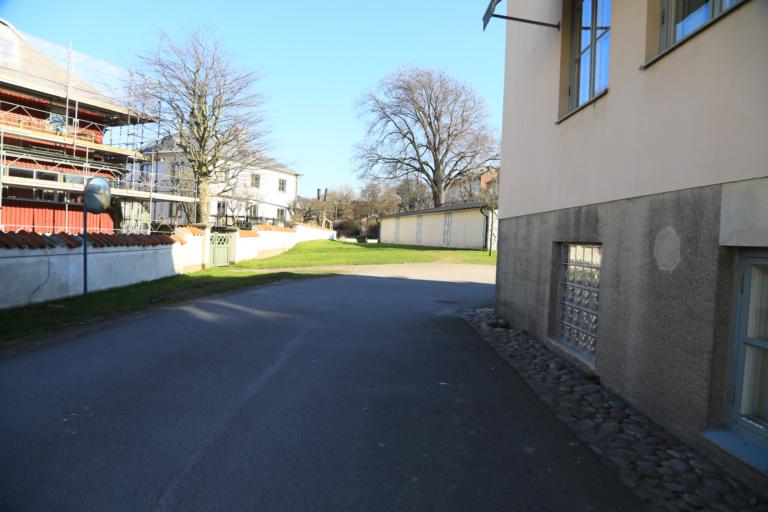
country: SE
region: Halland
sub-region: Varbergs Kommun
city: Varberg
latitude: 57.1059
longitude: 12.2447
